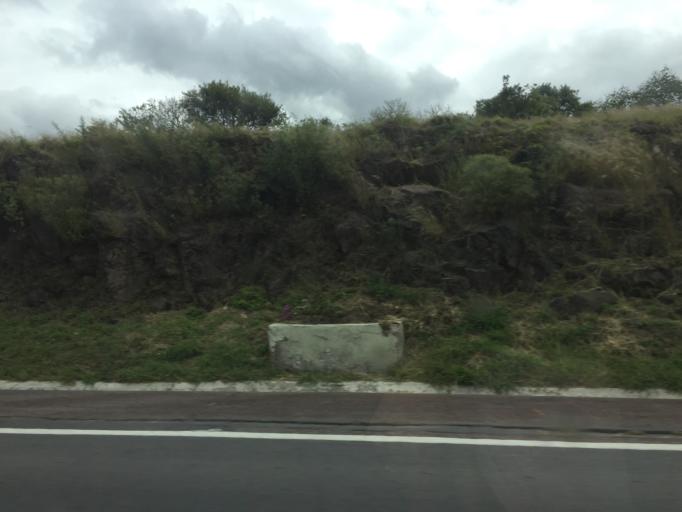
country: MX
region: Jalisco
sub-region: Tonala
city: Mismaloya (Fraccionamiento Pedregal de Santa Martha)
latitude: 20.6028
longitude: -103.1440
